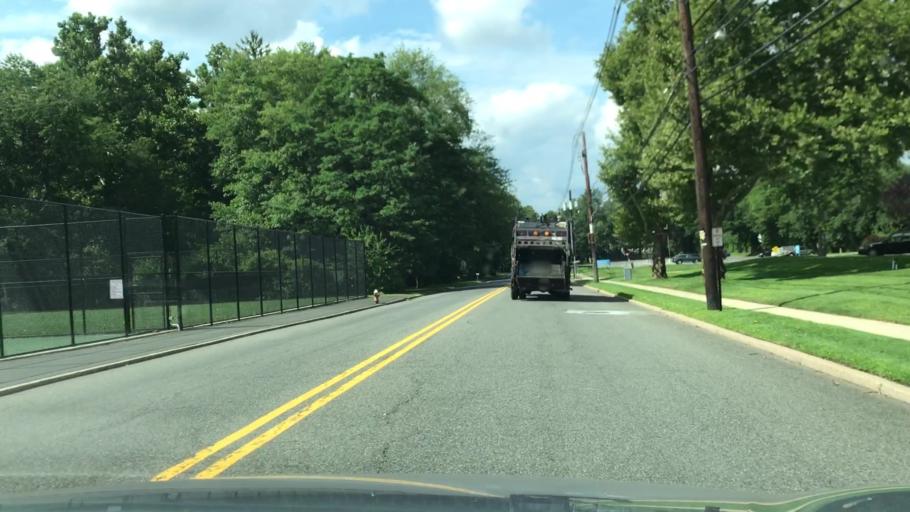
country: US
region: New Jersey
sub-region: Bergen County
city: Demarest
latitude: 40.9635
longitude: -73.9745
